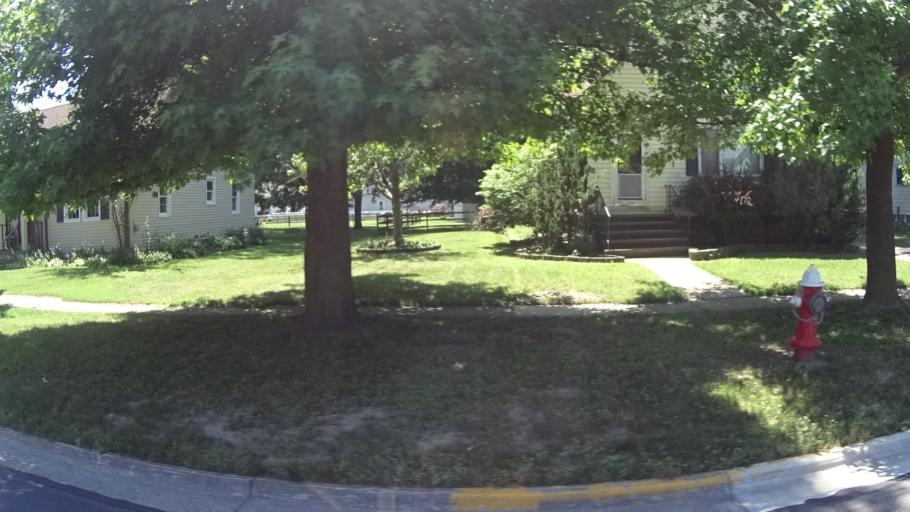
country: US
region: Ohio
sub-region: Erie County
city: Huron
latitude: 41.3924
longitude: -82.5646
